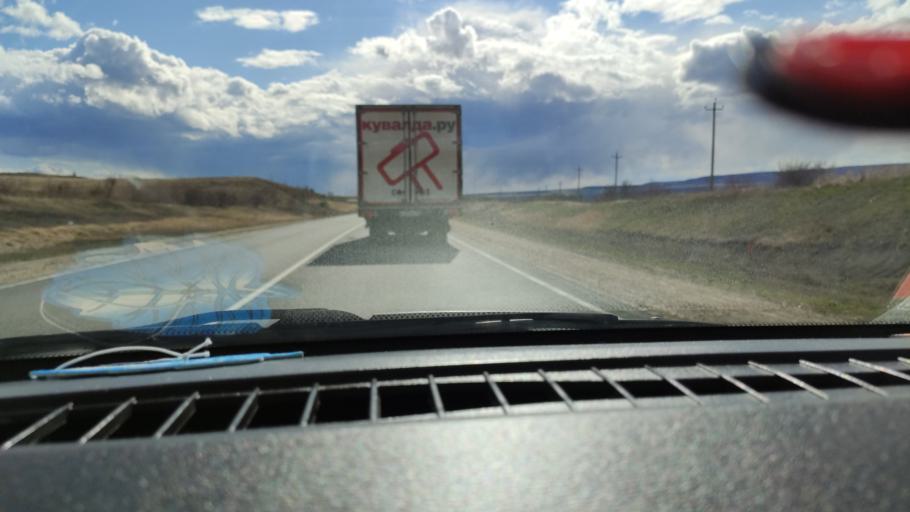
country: RU
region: Saratov
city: Alekseyevka
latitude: 52.3320
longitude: 47.9226
